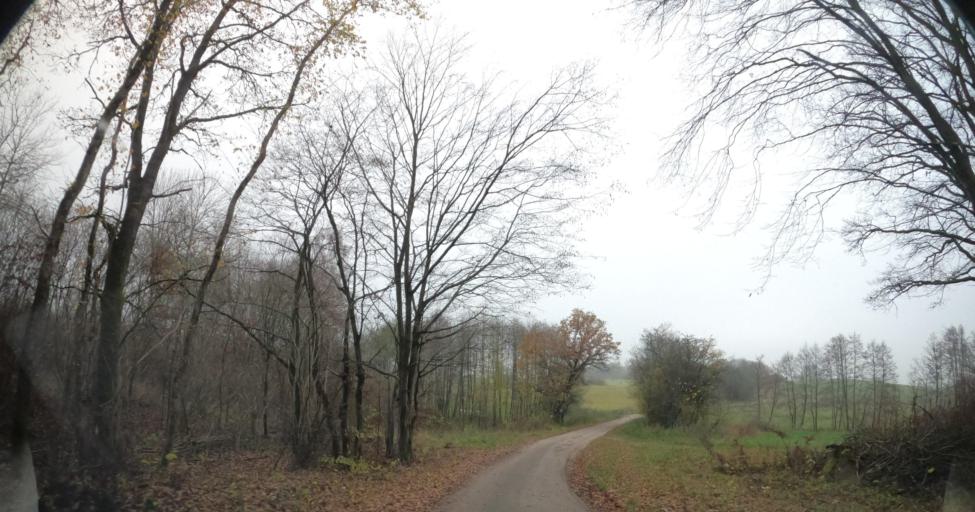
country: PL
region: West Pomeranian Voivodeship
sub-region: Powiat drawski
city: Drawsko Pomorskie
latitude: 53.5844
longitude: 15.8008
